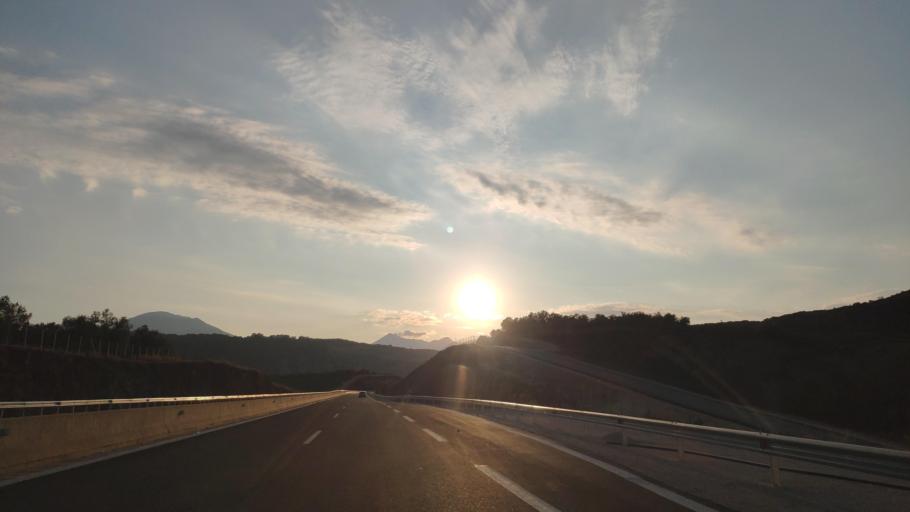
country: GR
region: West Greece
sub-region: Nomos Aitolias kai Akarnanias
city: Stanos
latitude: 38.7722
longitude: 21.1685
